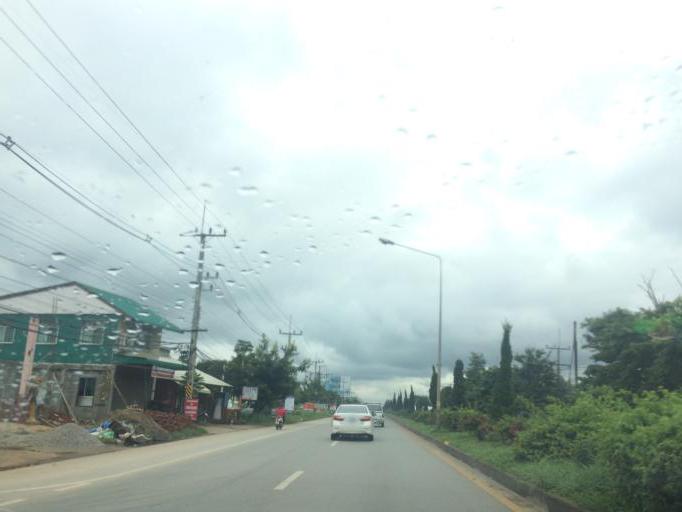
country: TH
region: Chiang Rai
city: Chiang Rai
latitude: 20.0088
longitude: 99.8681
